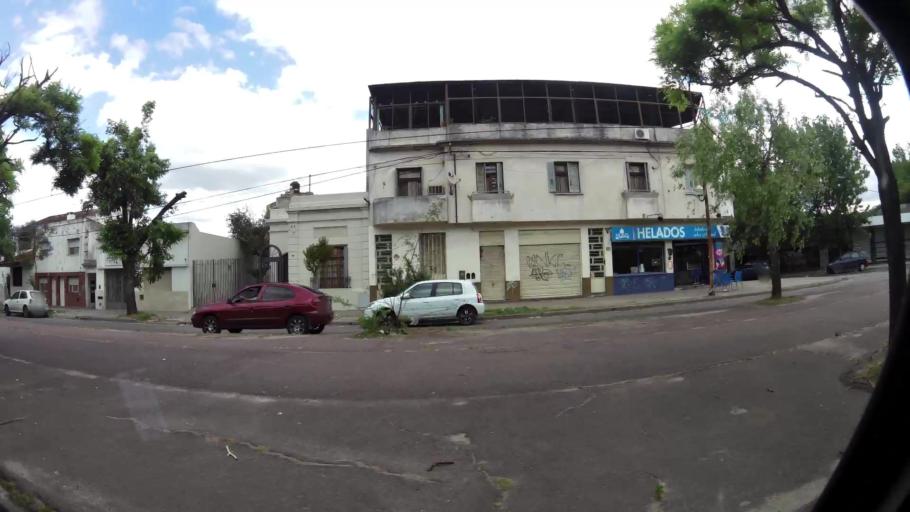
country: AR
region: Buenos Aires
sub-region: Partido de La Plata
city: La Plata
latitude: -34.9148
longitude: -57.9306
